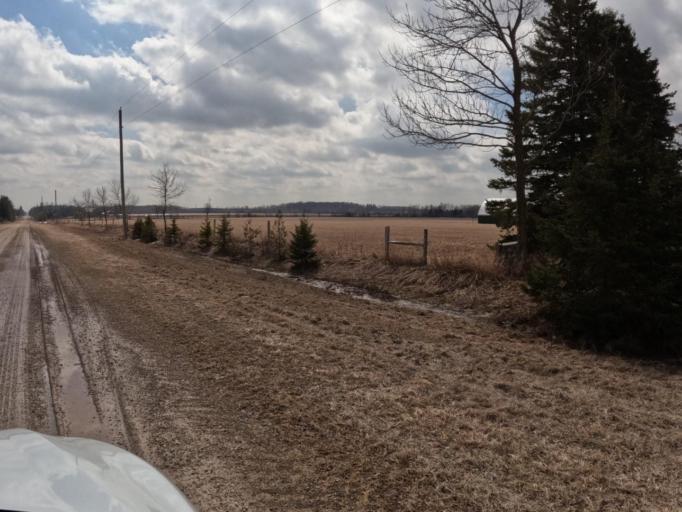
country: CA
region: Ontario
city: Shelburne
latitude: 44.0201
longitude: -80.3295
